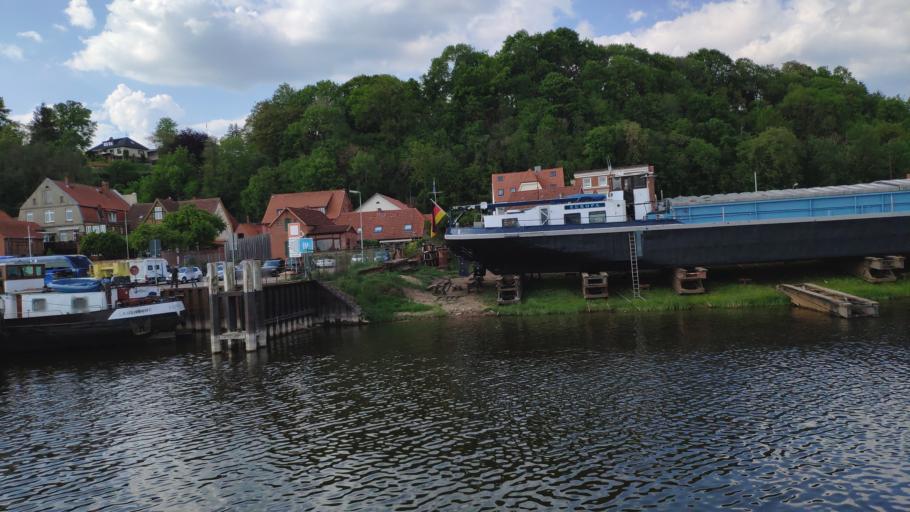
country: DE
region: Schleswig-Holstein
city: Lauenburg
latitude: 53.3697
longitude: 10.5604
